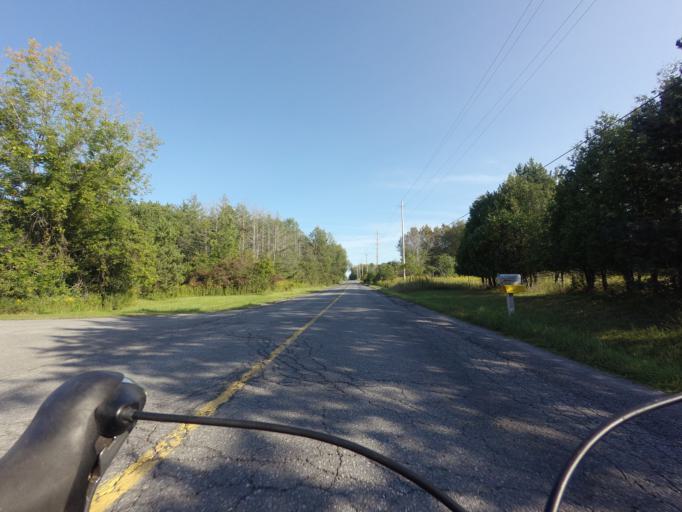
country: CA
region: Ontario
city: Bells Corners
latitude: 45.4616
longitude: -76.0226
